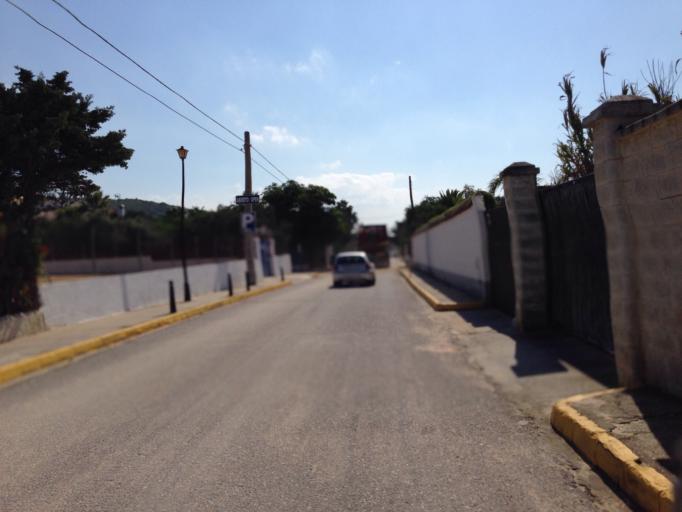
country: ES
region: Andalusia
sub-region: Provincia de Cadiz
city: Vejer de la Frontera
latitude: 36.1844
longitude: -6.0072
